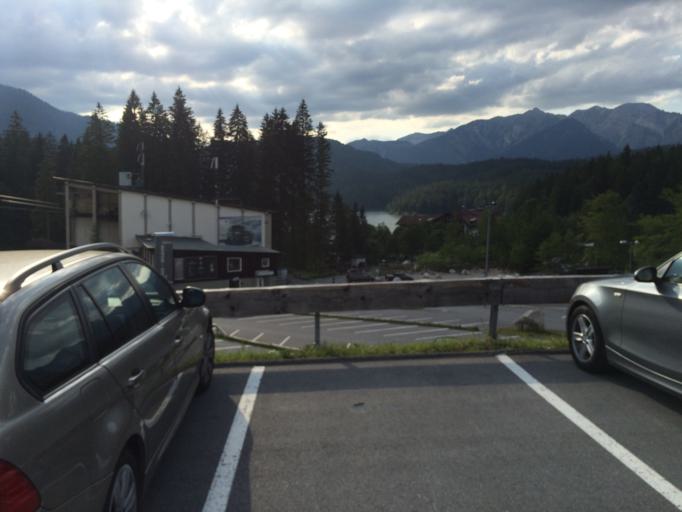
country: DE
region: Bavaria
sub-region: Upper Bavaria
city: Grainau
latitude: 47.4560
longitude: 10.9934
